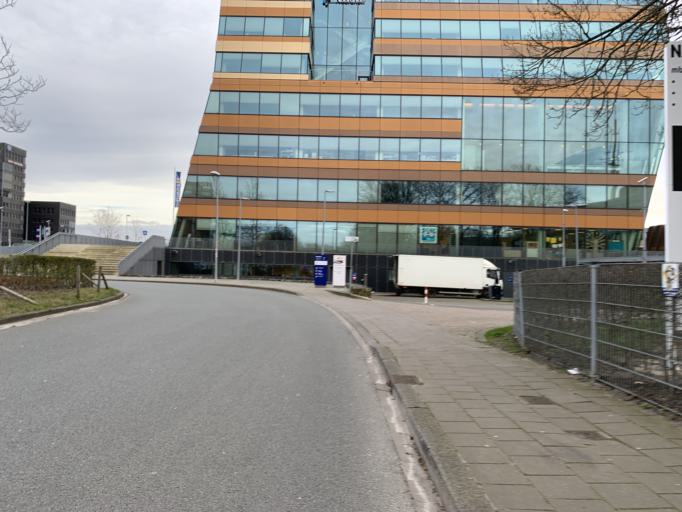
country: NL
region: Groningen
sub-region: Gemeente Groningen
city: Oosterpark
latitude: 53.2095
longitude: 6.5875
